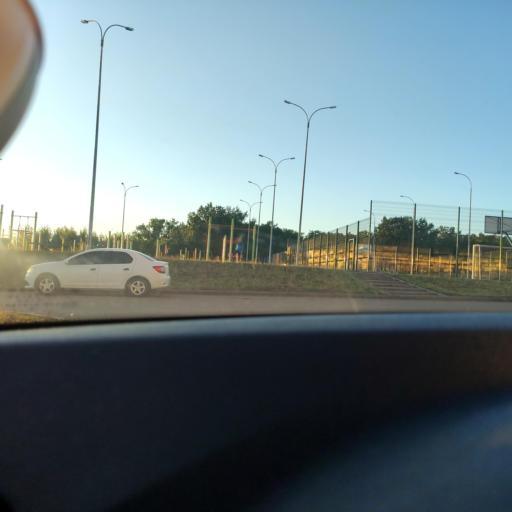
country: RU
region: Samara
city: Petra-Dubrava
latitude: 53.3042
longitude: 50.3344
